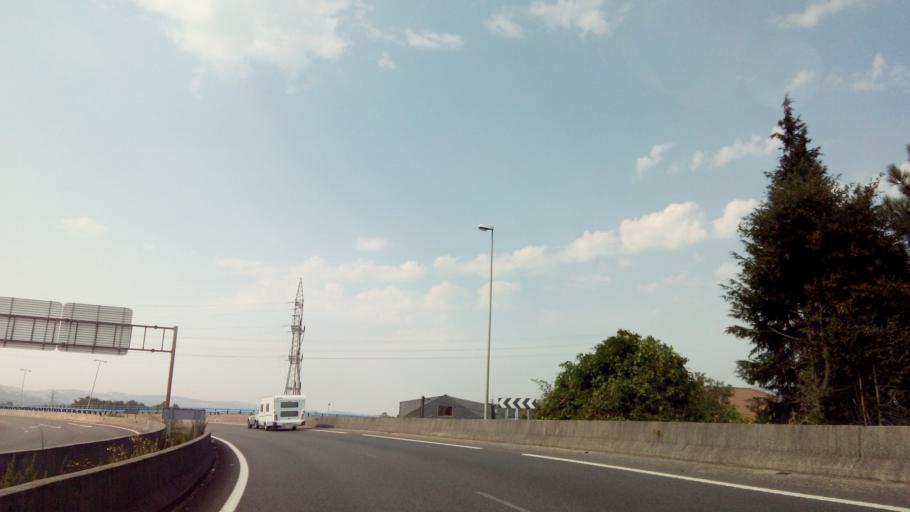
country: ES
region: Galicia
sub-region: Provincia de Pontevedra
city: Porrino
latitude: 42.1358
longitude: -8.6224
